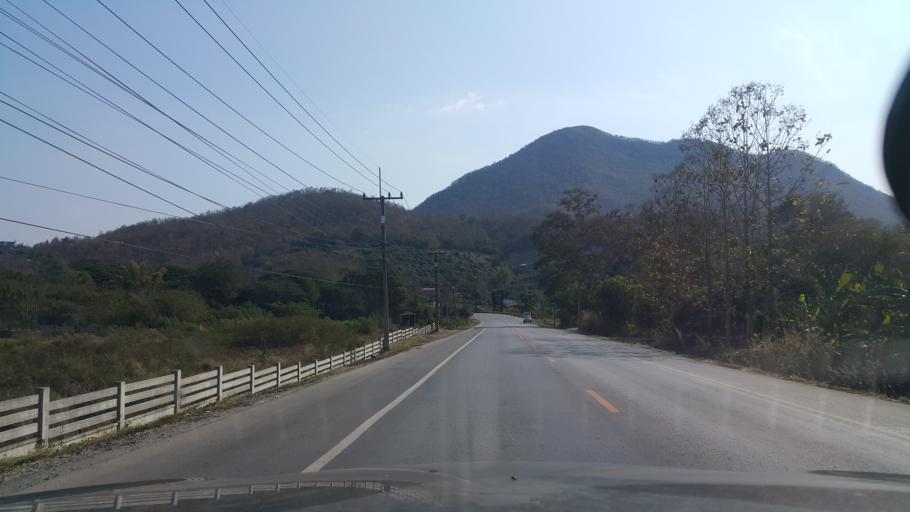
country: LA
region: Vientiane
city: Muang Sanakham
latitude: 17.8981
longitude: 101.7134
